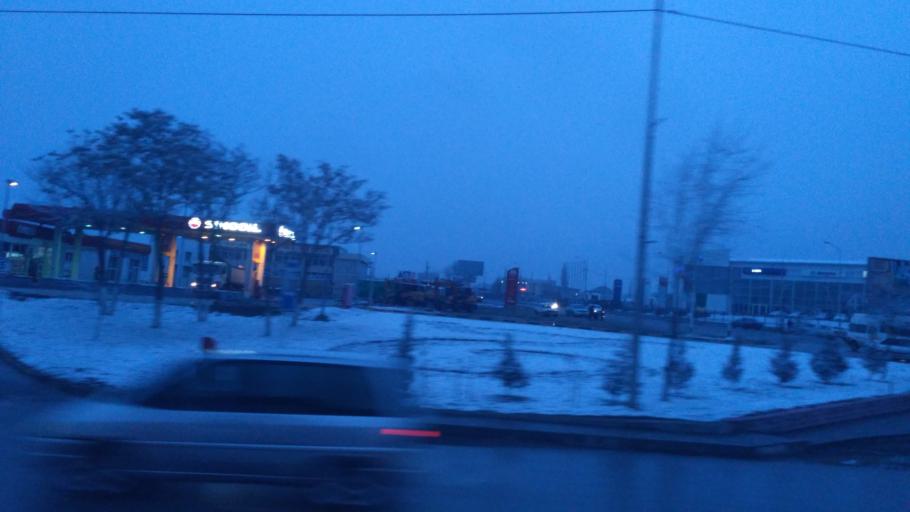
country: KZ
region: Ongtustik Qazaqstan
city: Shymkent
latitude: 42.3522
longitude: 69.5303
